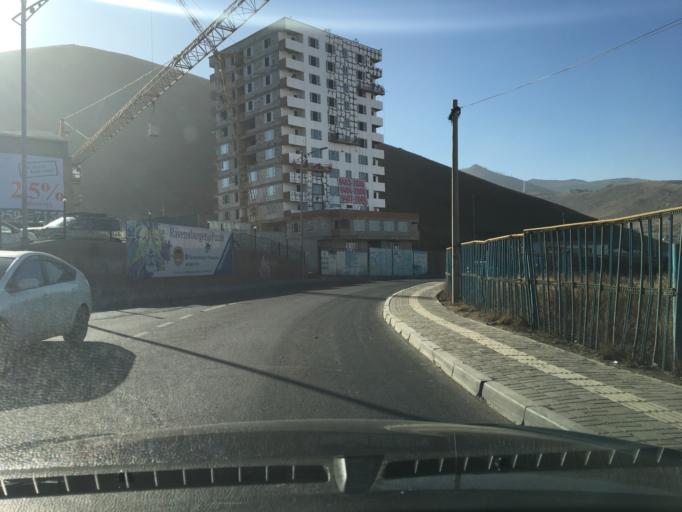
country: MN
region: Ulaanbaatar
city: Ulaanbaatar
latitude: 47.8865
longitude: 106.9049
